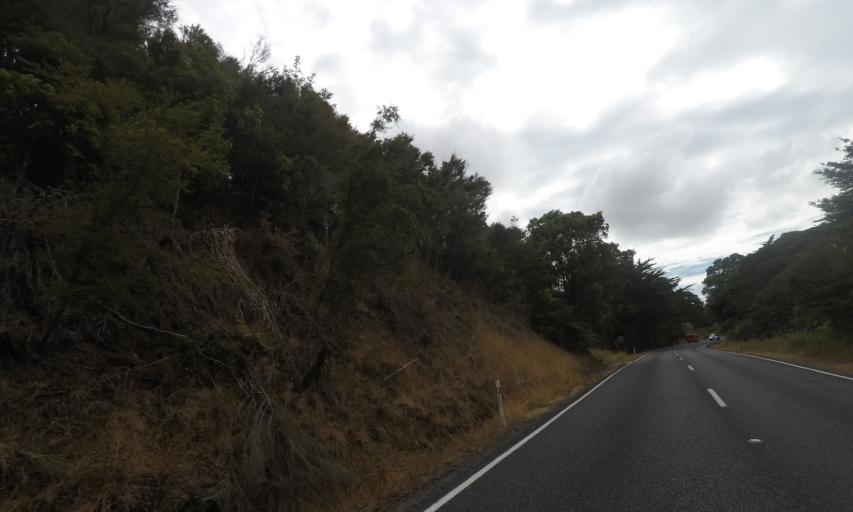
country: NZ
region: Northland
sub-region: Whangarei
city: Ruakaka
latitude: -35.7637
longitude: 174.4697
